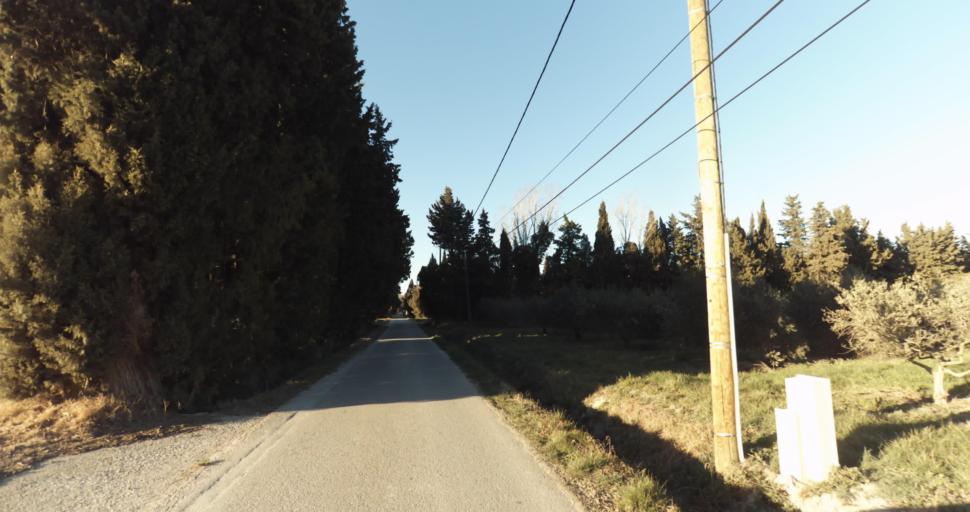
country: FR
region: Provence-Alpes-Cote d'Azur
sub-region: Departement des Bouches-du-Rhone
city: Barbentane
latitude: 43.9094
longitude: 4.7576
